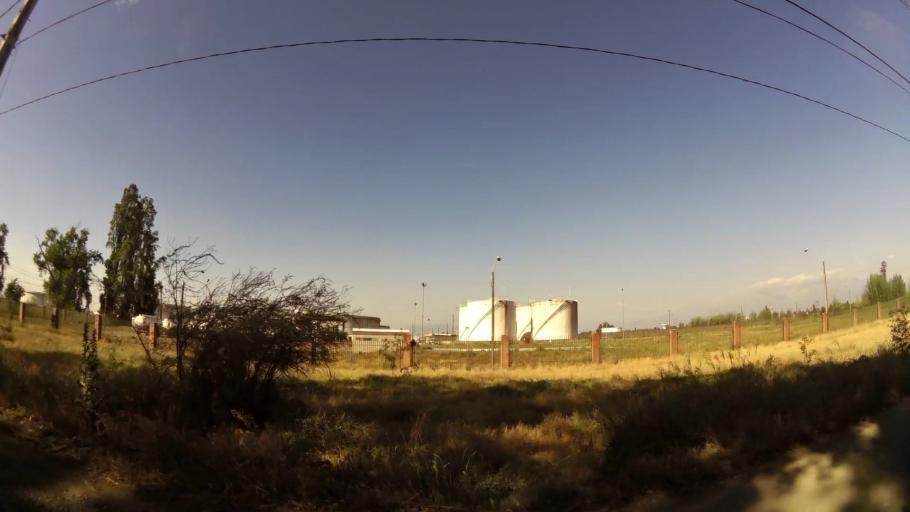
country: CL
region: Santiago Metropolitan
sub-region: Provincia de Maipo
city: San Bernardo
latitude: -33.5455
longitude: -70.7565
